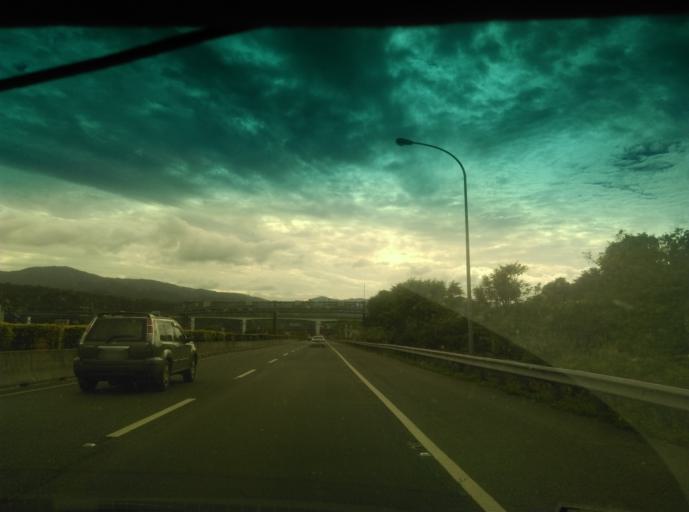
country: TW
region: Taiwan
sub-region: Keelung
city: Keelung
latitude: 25.1105
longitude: 121.7263
